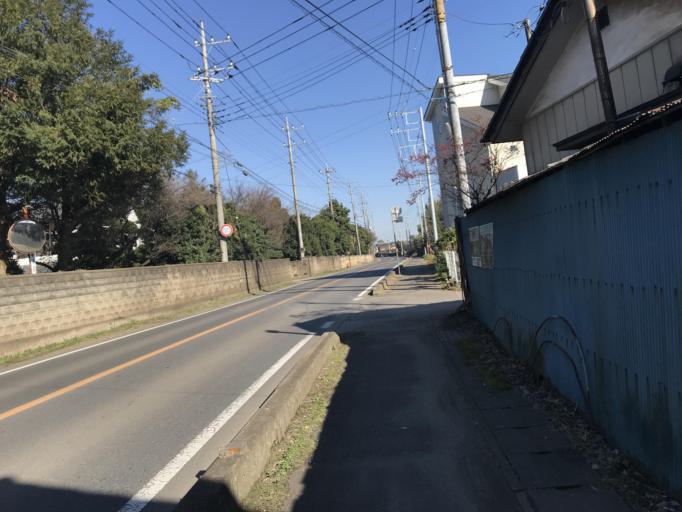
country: JP
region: Ibaraki
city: Yuki
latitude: 36.2690
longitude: 139.8448
